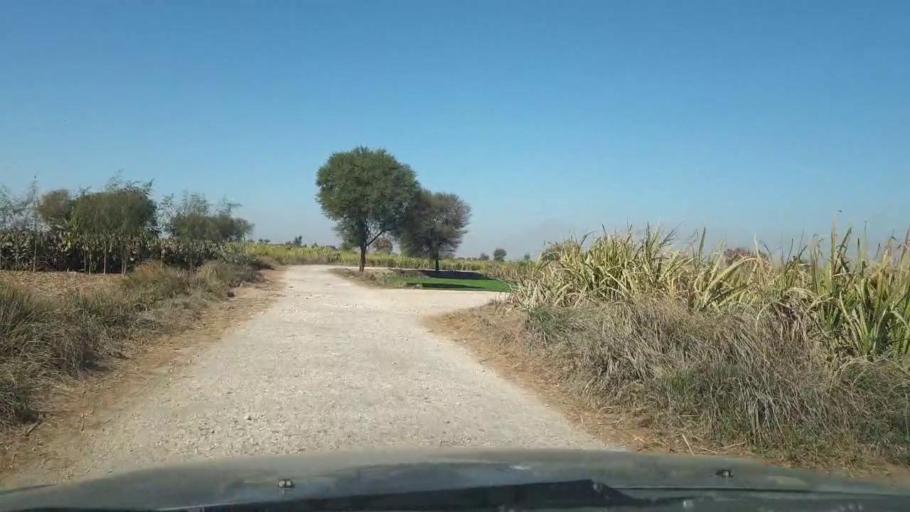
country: PK
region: Sindh
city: Ghotki
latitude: 28.0492
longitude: 69.2411
